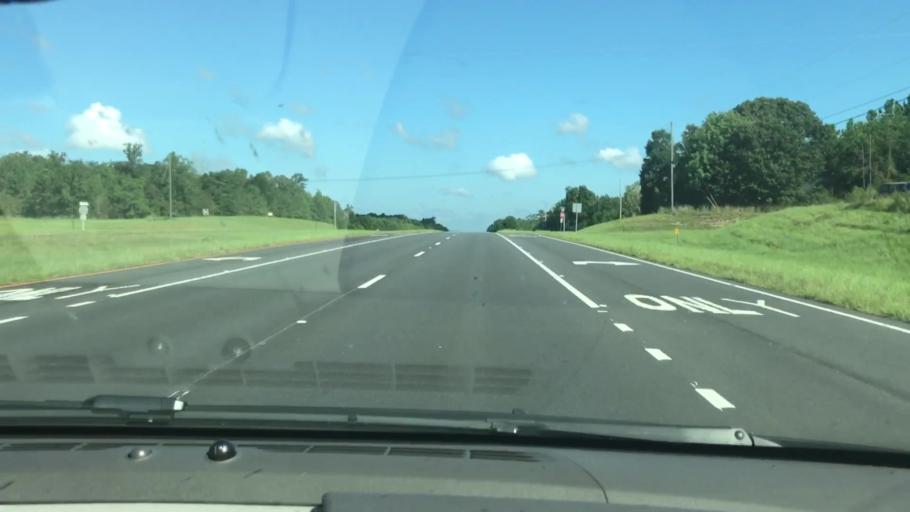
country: US
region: Alabama
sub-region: Barbour County
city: Eufaula
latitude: 32.0377
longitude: -85.1259
